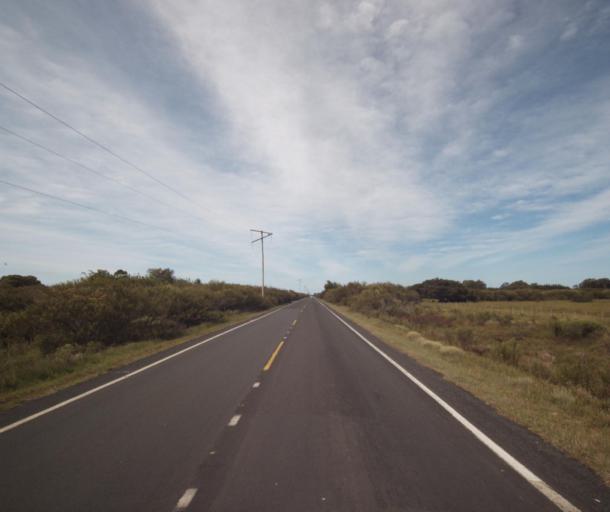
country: BR
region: Rio Grande do Sul
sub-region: Rio Grande
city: Rio Grande
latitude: -31.9194
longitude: -51.9465
